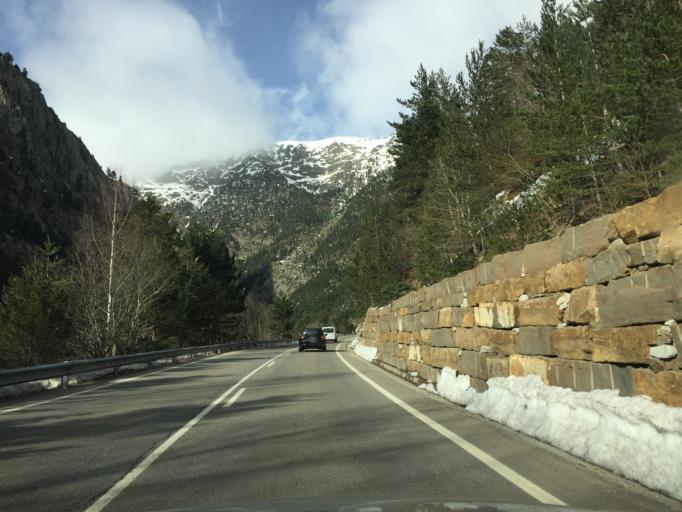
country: ES
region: Aragon
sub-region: Provincia de Huesca
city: Bielsa
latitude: 42.7072
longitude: 0.2018
